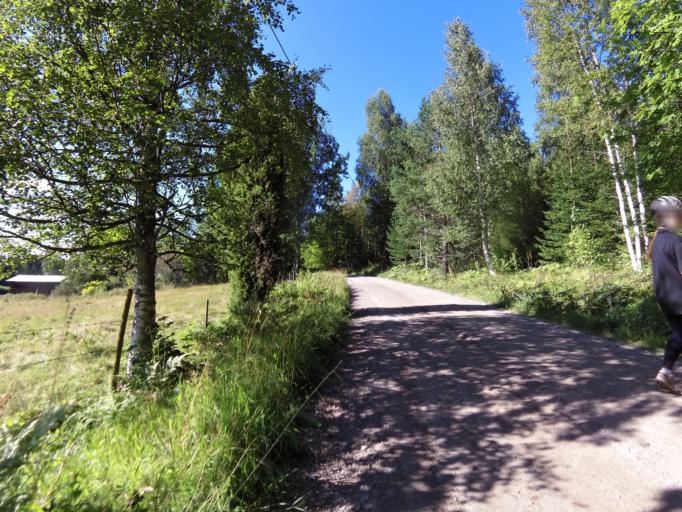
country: SE
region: Gaevleborg
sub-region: Hofors Kommun
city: Hofors
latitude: 60.5327
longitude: 16.4125
